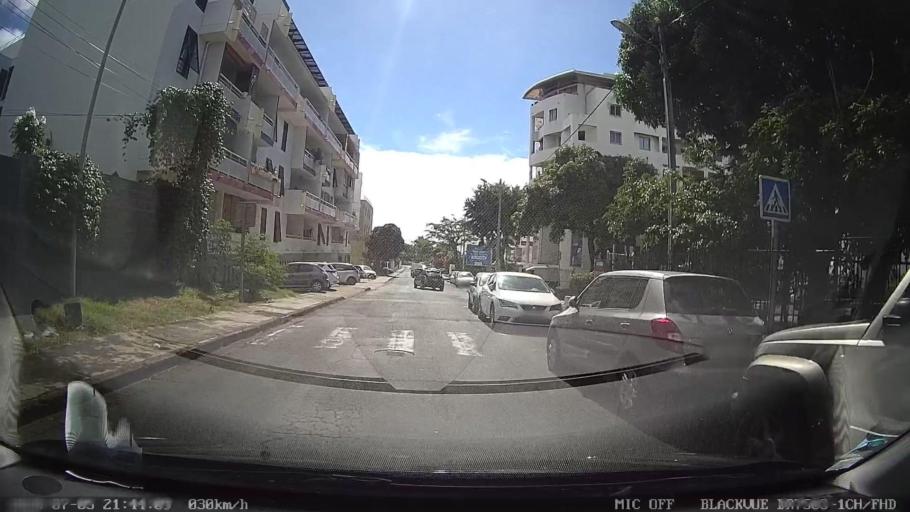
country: RE
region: Reunion
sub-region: Reunion
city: Saint-Denis
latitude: -20.8879
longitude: 55.4796
